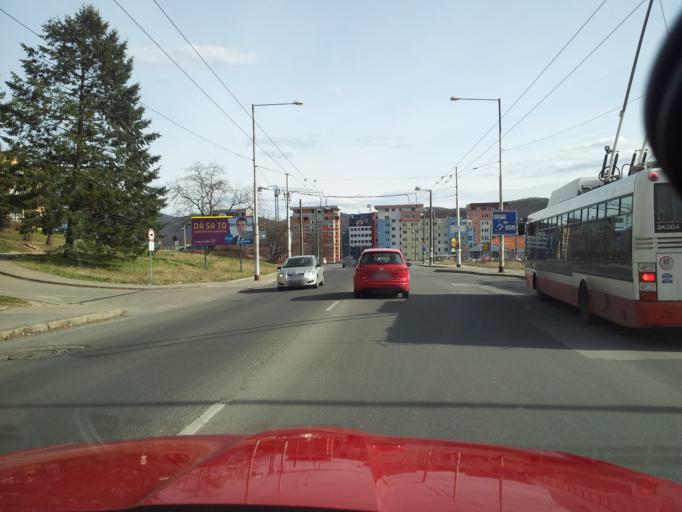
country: SK
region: Banskobystricky
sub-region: Okres Banska Bystrica
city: Banska Bystrica
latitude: 48.7401
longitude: 19.1268
